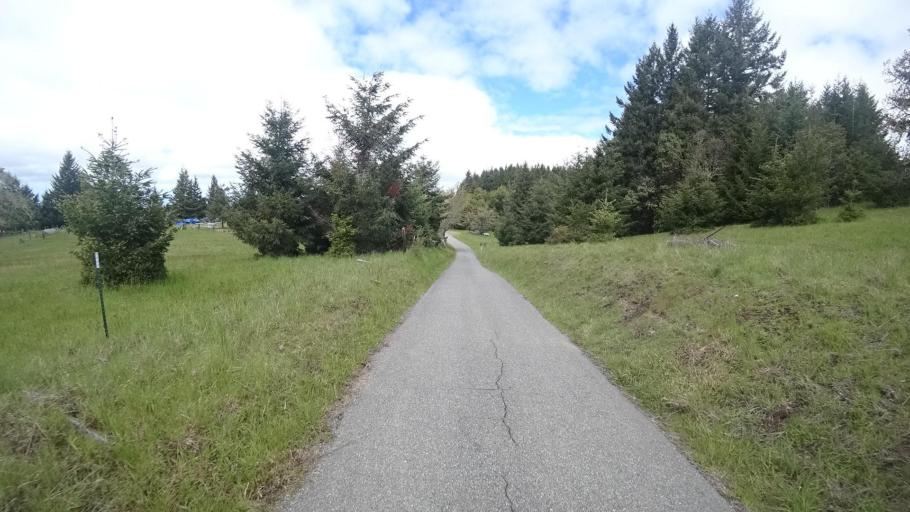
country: US
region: California
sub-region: Humboldt County
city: Blue Lake
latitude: 40.7907
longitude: -123.9686
